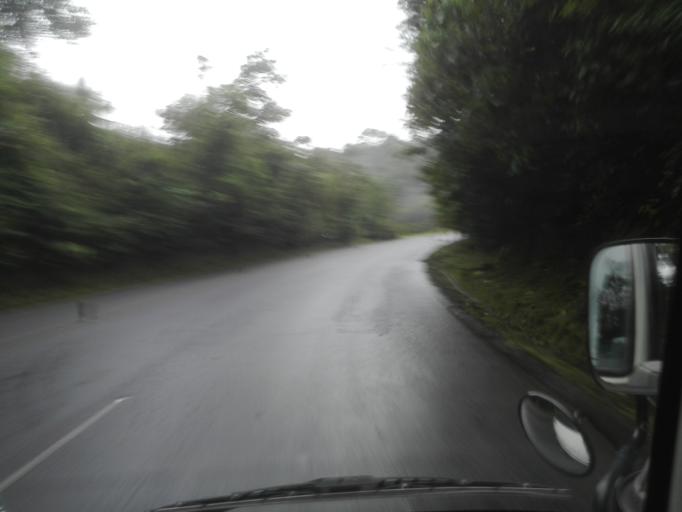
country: CR
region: San Jose
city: Dulce Nombre de Jesus
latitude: 10.1969
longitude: -83.9012
